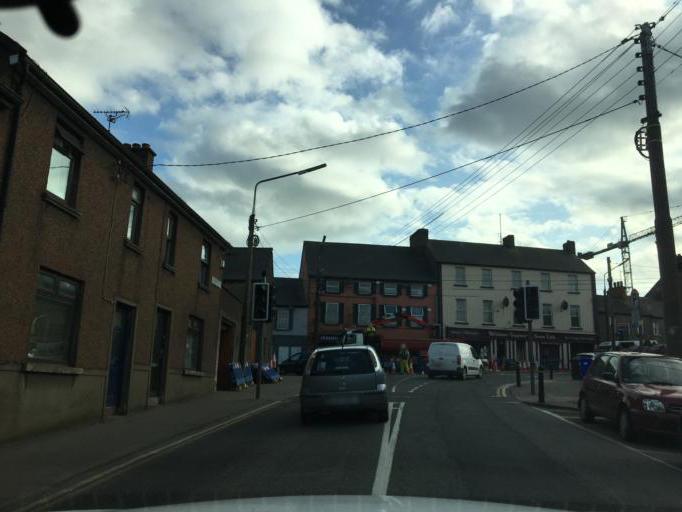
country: IE
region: Leinster
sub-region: Loch Garman
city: Loch Garman
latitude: 52.3405
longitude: -6.4706
